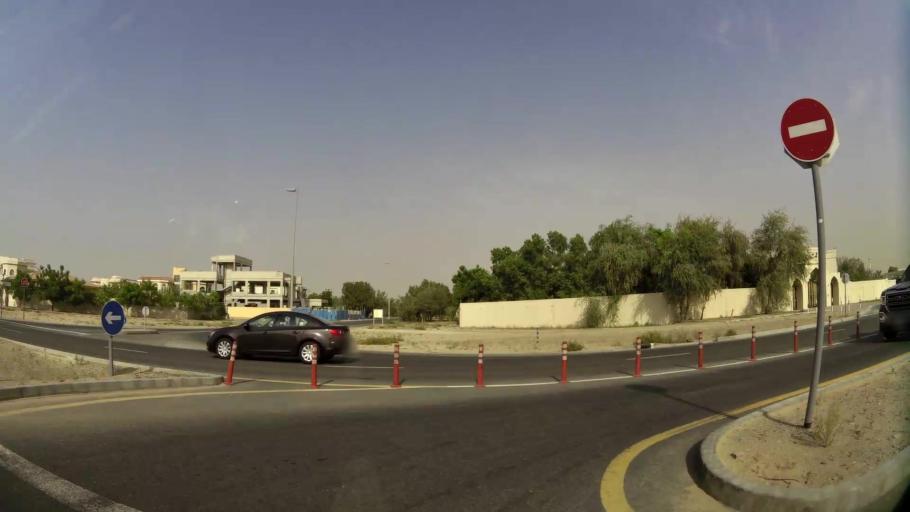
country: AE
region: Ash Shariqah
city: Sharjah
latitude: 25.2525
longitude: 55.4549
